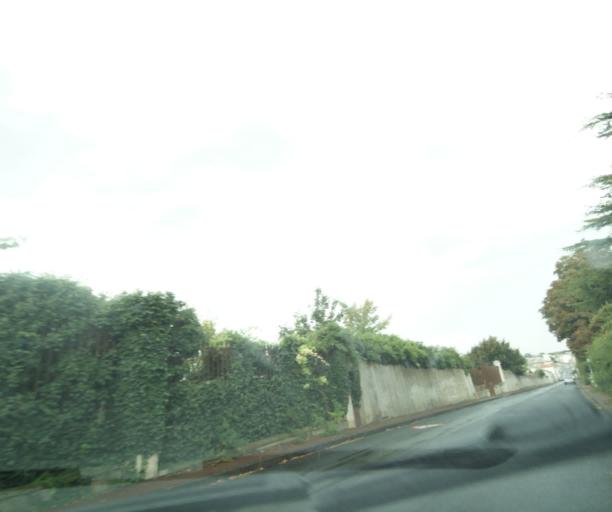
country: FR
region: Poitou-Charentes
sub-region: Departement de la Charente-Maritime
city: Tonnay-Charente
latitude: 45.9416
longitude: -0.8855
